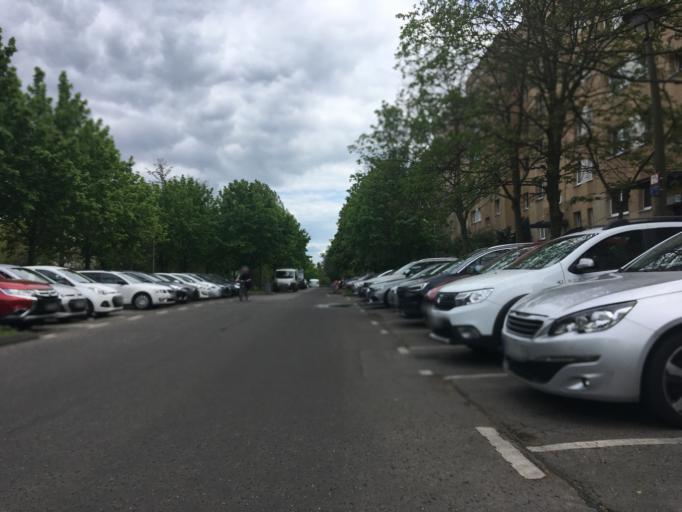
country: DE
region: Berlin
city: Marzahn
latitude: 52.5546
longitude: 13.5771
